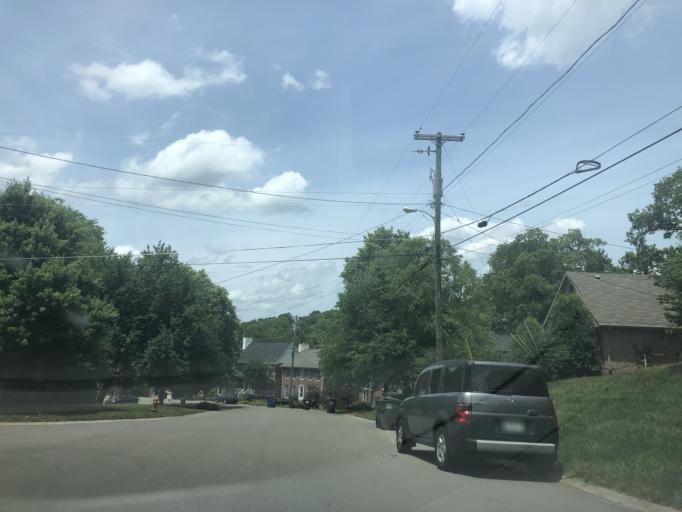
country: US
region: Tennessee
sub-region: Cheatham County
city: Pegram
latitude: 36.0493
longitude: -86.9591
